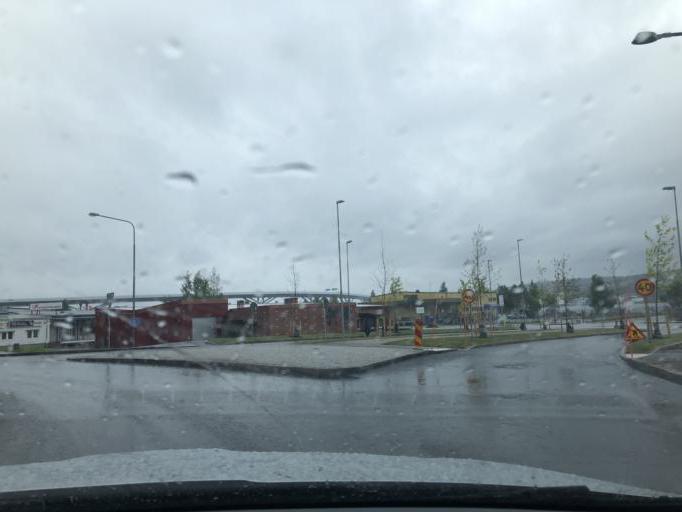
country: SE
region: Vaesternorrland
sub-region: Sundsvalls Kommun
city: Sundsvall
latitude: 62.3951
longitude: 17.3276
